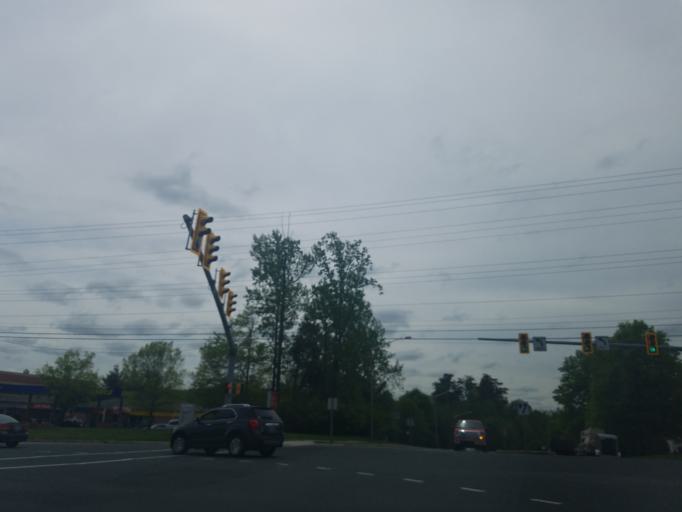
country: US
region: Virginia
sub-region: Fairfax County
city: Centreville
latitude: 38.8349
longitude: -77.4566
